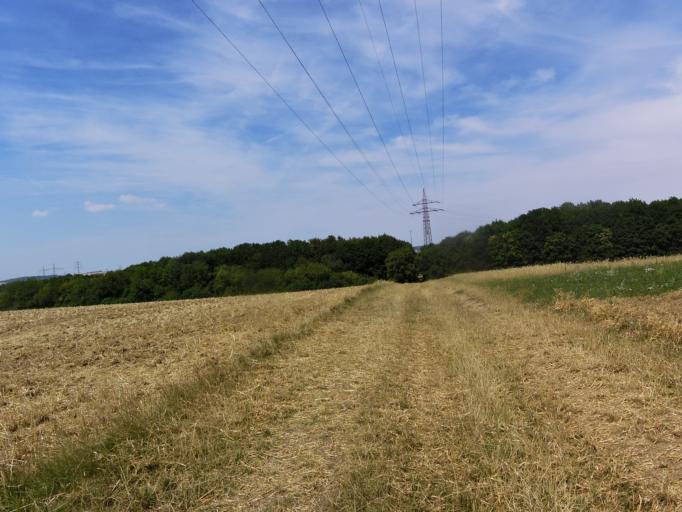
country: DE
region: Bavaria
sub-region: Regierungsbezirk Unterfranken
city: Rottendorf
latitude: 49.7945
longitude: 10.0103
